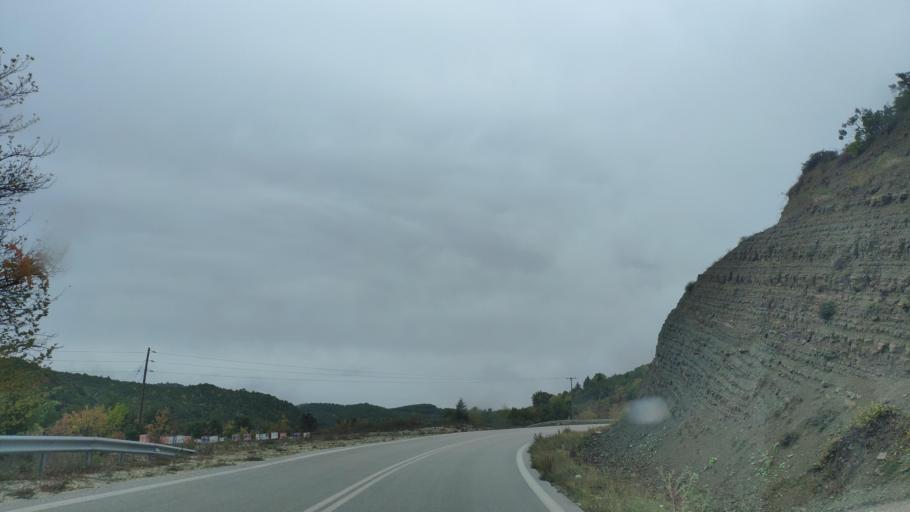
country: GR
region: Epirus
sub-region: Nomos Thesprotias
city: Paramythia
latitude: 39.4877
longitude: 20.6717
